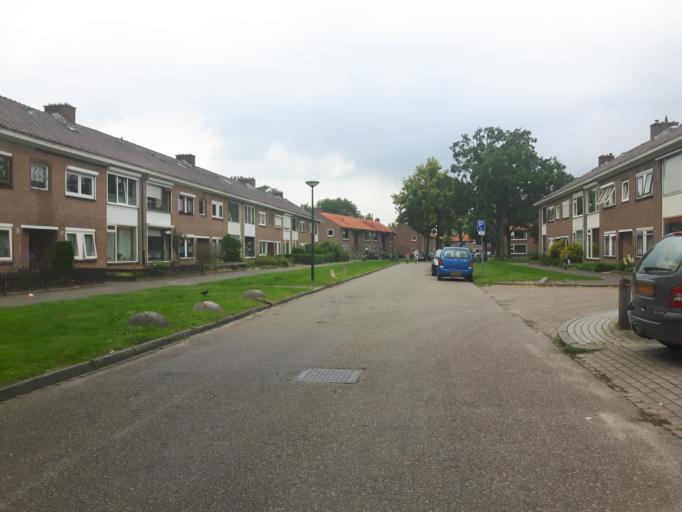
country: NL
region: Overijssel
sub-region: Gemeente Enschede
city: Enschede
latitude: 52.2121
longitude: 6.8646
